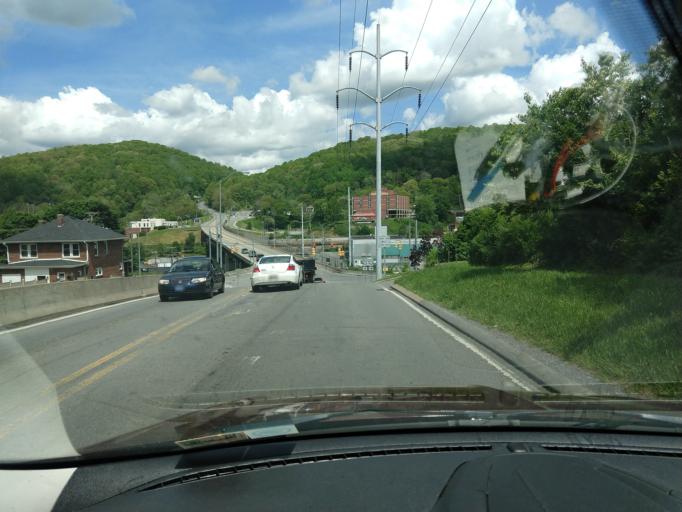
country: US
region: West Virginia
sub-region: Mercer County
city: Bluefield
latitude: 37.2619
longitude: -81.2364
